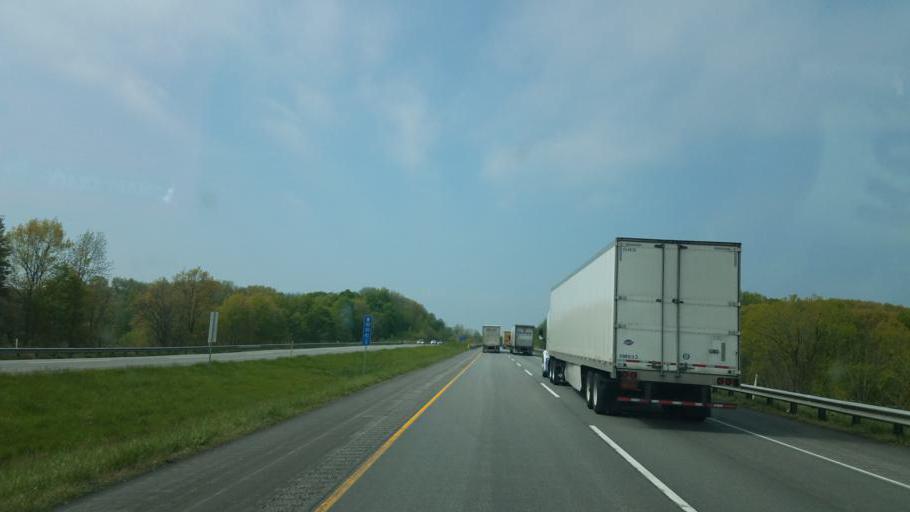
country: US
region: Indiana
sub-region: LaPorte County
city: Westville
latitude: 41.6021
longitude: -86.8629
